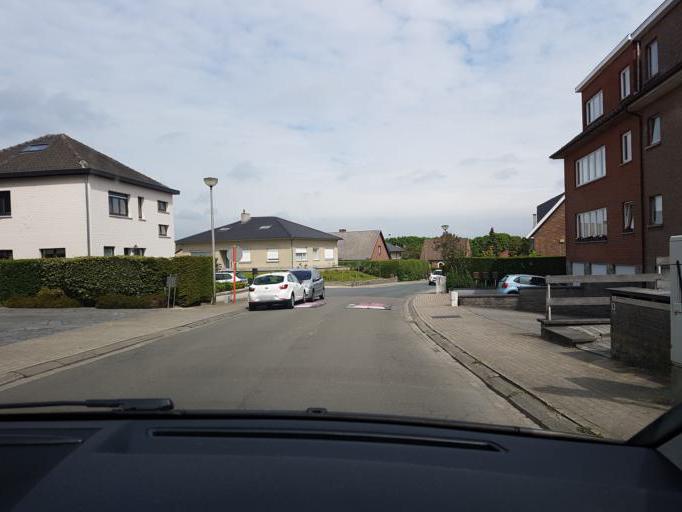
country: BE
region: Flanders
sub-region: Provincie Vlaams-Brabant
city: Dilbeek
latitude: 50.8653
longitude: 4.2648
